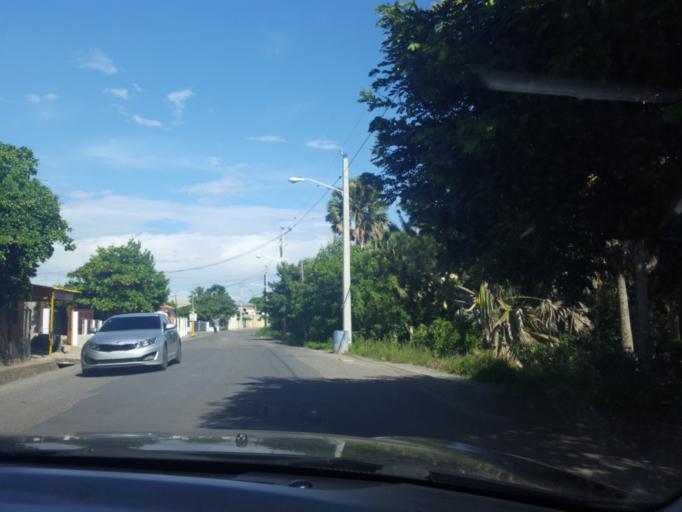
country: DO
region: La Vega
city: Rio Verde Arriba
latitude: 19.3678
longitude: -70.6064
